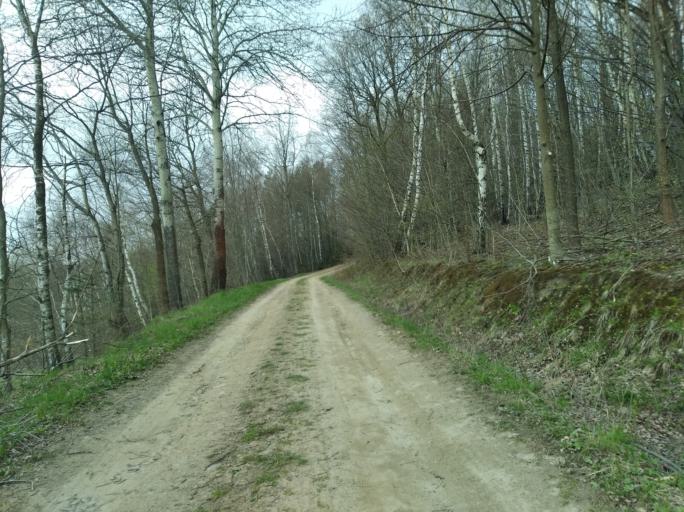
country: PL
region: Subcarpathian Voivodeship
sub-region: Powiat strzyzowski
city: Jawornik
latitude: 49.8184
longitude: 21.8969
